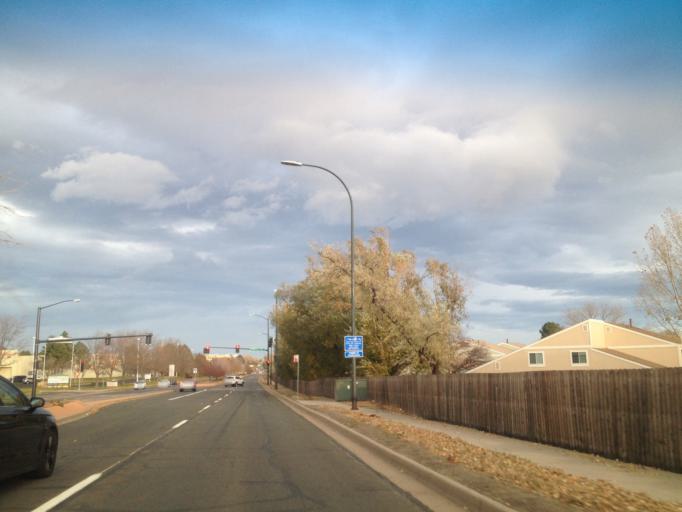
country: US
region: Colorado
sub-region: Adams County
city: Westminster
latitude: 39.8564
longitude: -105.0752
